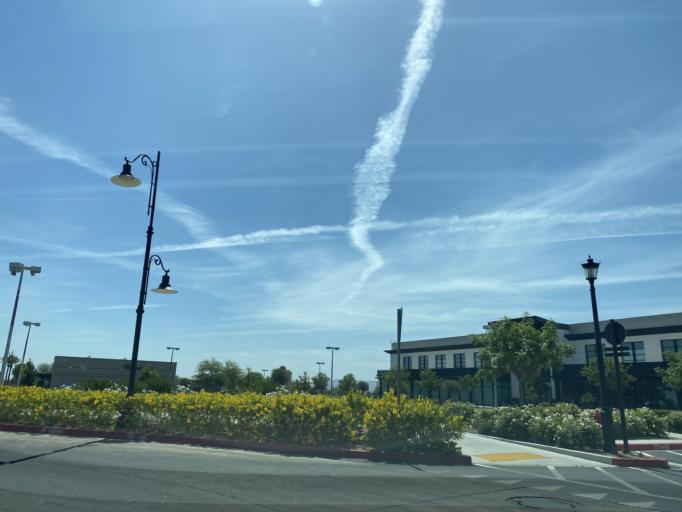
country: US
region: Nevada
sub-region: Clark County
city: Paradise
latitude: 36.0697
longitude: -115.1752
